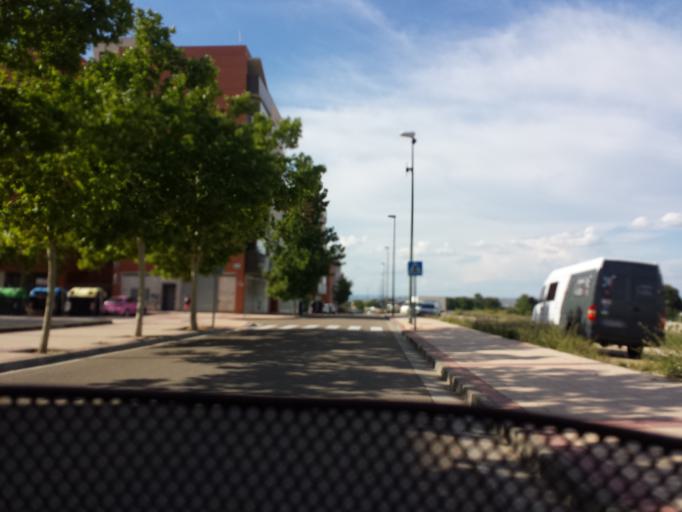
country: ES
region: Aragon
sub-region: Provincia de Zaragoza
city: Montecanal
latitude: 41.6361
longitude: -0.9445
